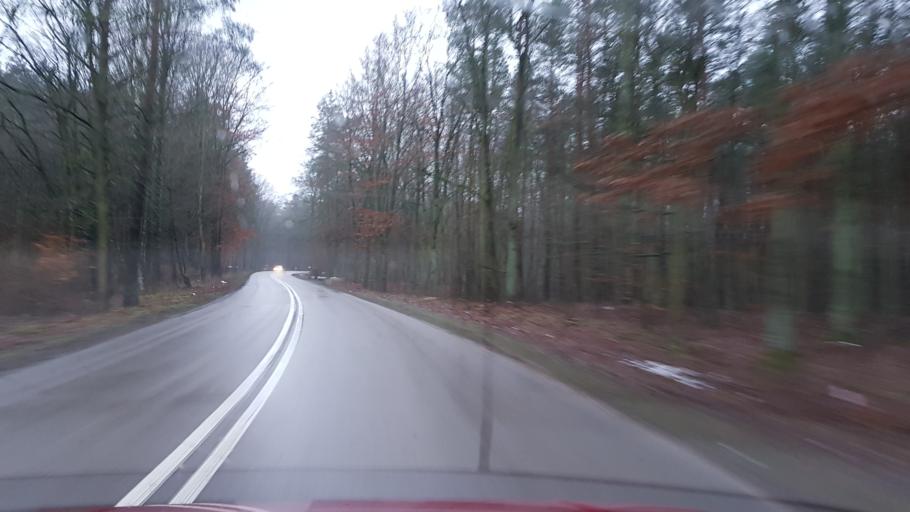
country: PL
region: West Pomeranian Voivodeship
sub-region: Powiat policki
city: Police
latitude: 53.5247
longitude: 14.5268
